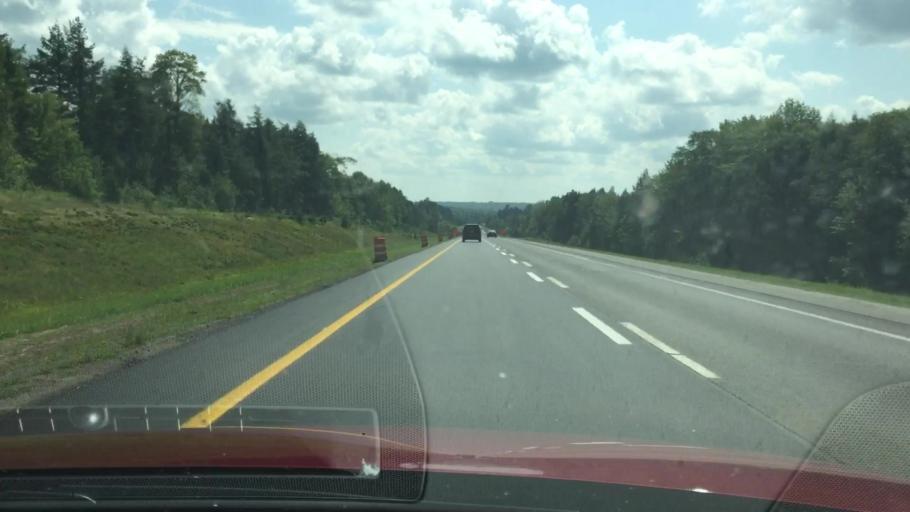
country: US
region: Maine
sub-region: Penobscot County
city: Medway
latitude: 45.6557
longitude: -68.4995
